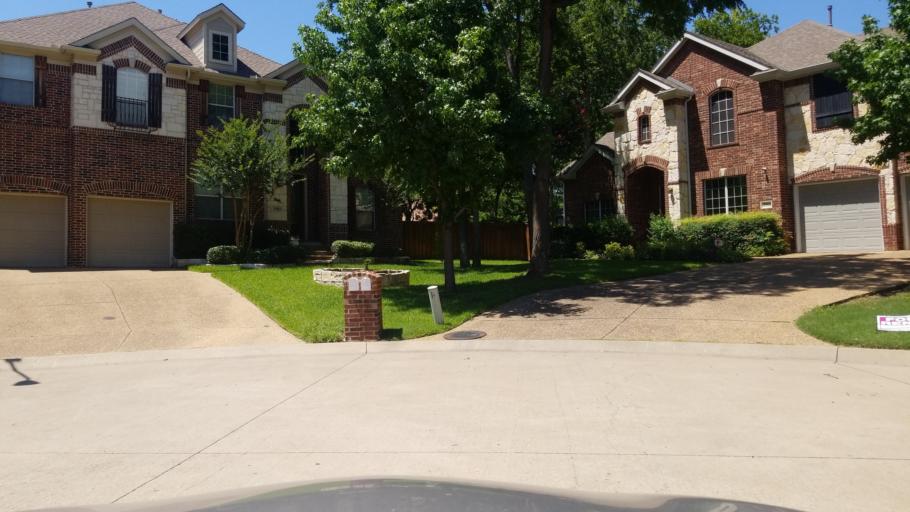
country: US
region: Texas
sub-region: Dallas County
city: Grand Prairie
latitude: 32.6838
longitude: -97.0018
